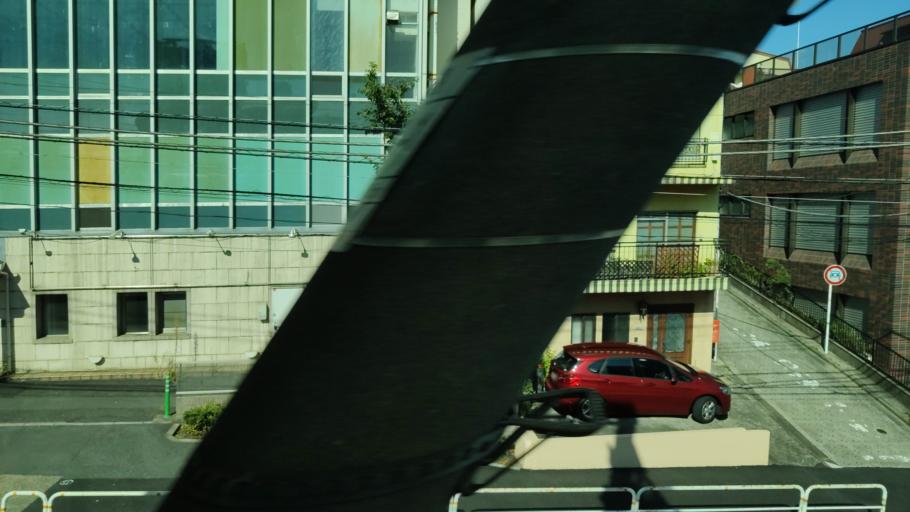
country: JP
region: Tokyo
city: Tokyo
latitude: 35.6295
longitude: 139.7186
